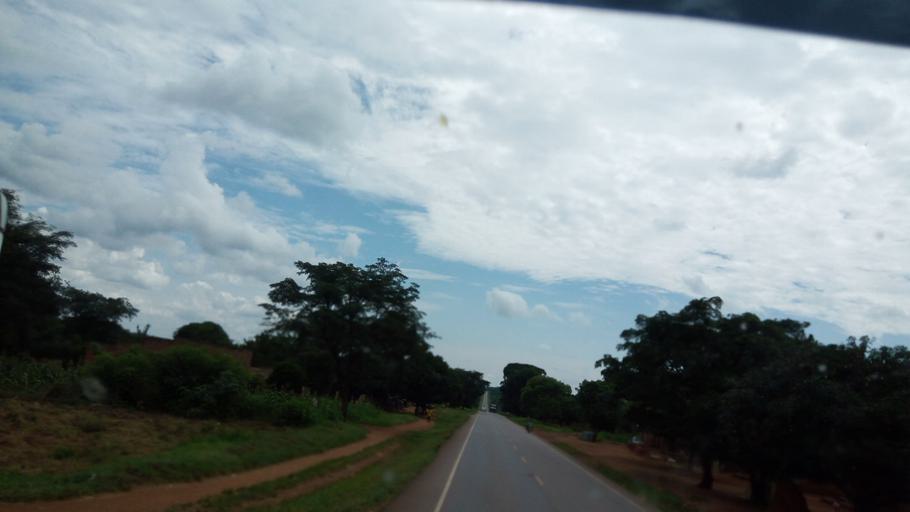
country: UG
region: Central Region
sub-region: Nakasongola District
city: Nakasongola
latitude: 1.1988
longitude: 32.4622
